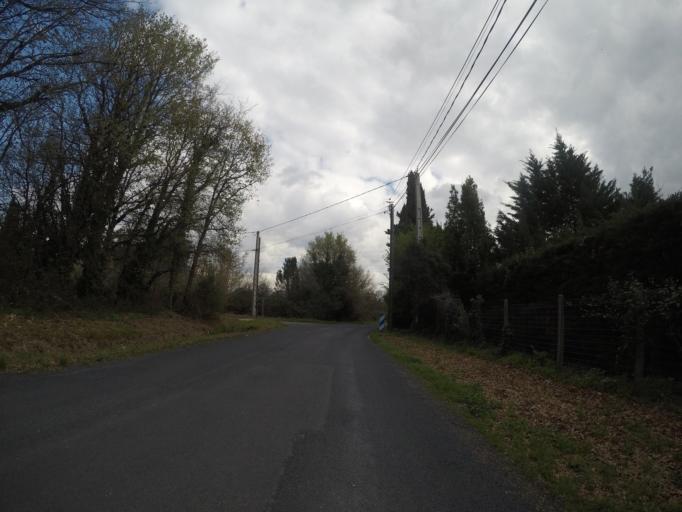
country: FR
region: Languedoc-Roussillon
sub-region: Departement des Pyrenees-Orientales
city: Le Soler
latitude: 42.6743
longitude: 2.7784
